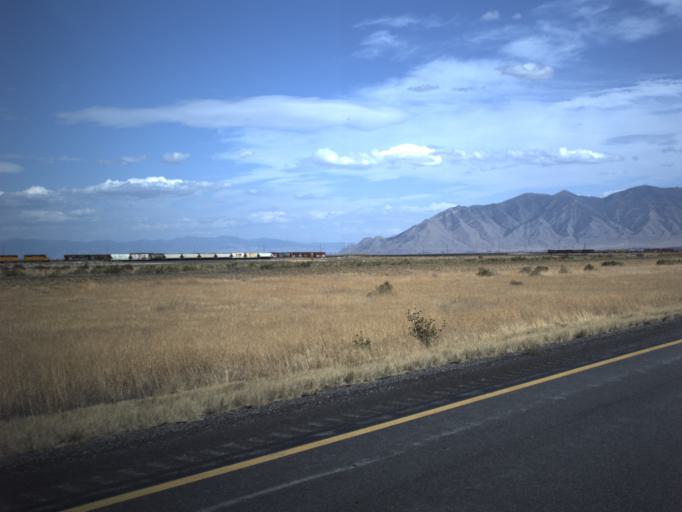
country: US
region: Utah
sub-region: Tooele County
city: Grantsville
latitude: 40.6877
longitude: -112.4551
